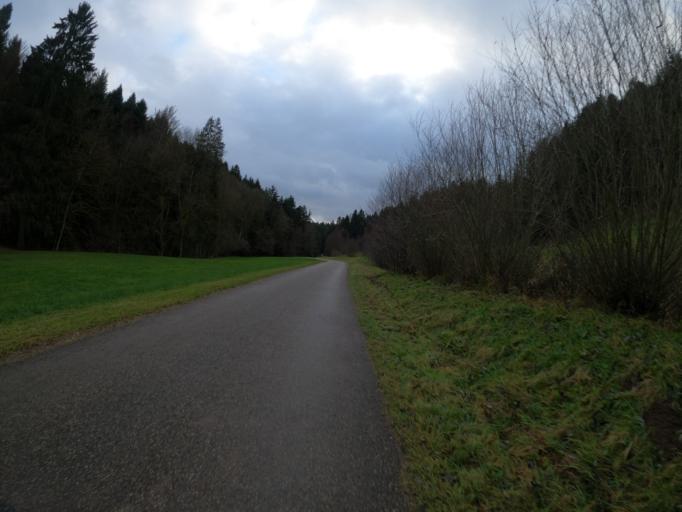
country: DE
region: Baden-Wuerttemberg
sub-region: Regierungsbezirk Stuttgart
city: Waschenbeuren
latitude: 48.7752
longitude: 9.7150
